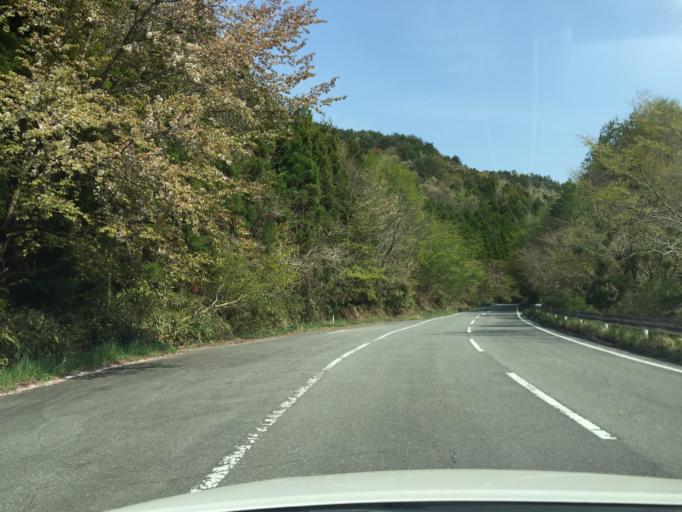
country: JP
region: Fukushima
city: Iwaki
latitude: 37.1850
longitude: 140.8514
